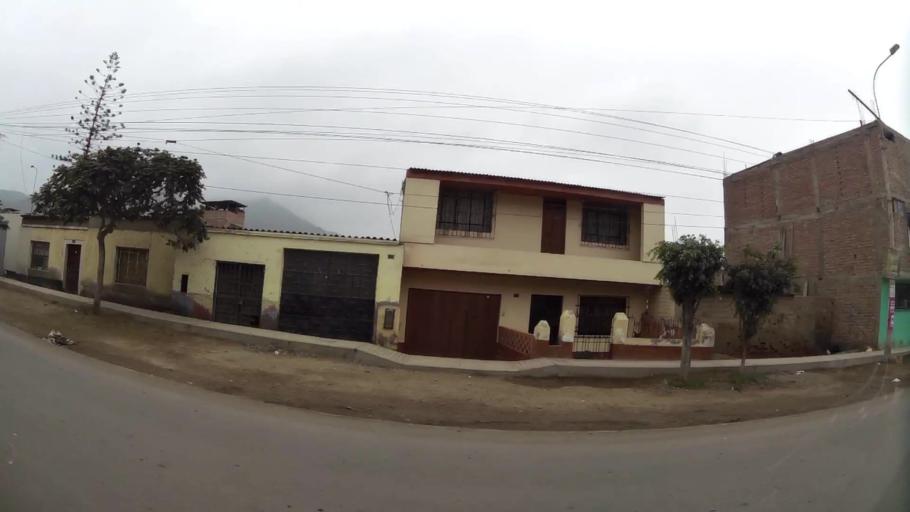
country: PE
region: Lima
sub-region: Lima
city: Surco
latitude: -12.2140
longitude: -76.9095
